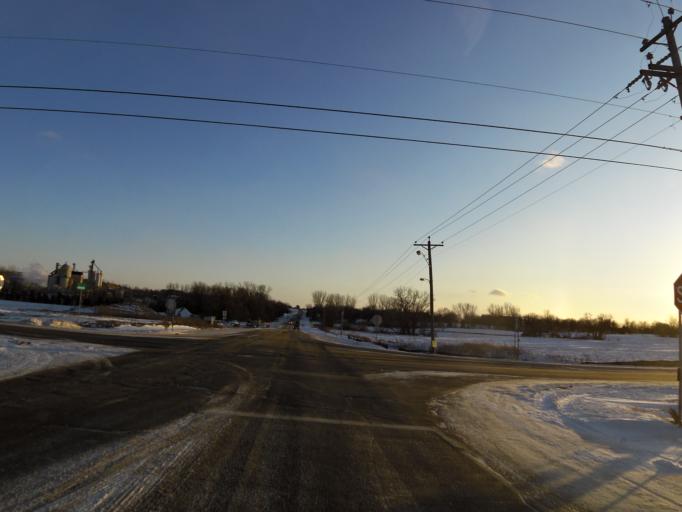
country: US
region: Minnesota
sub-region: Washington County
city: Lake Elmo
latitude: 44.9454
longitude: -92.8831
